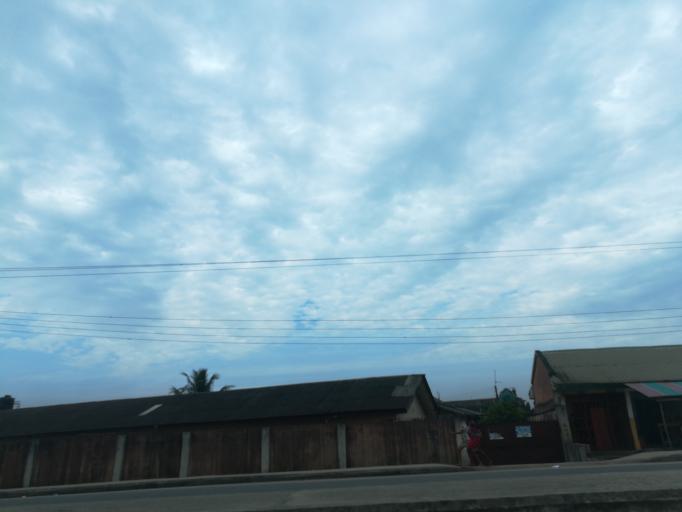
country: NG
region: Rivers
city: Port Harcourt
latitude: 4.8127
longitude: 6.9446
